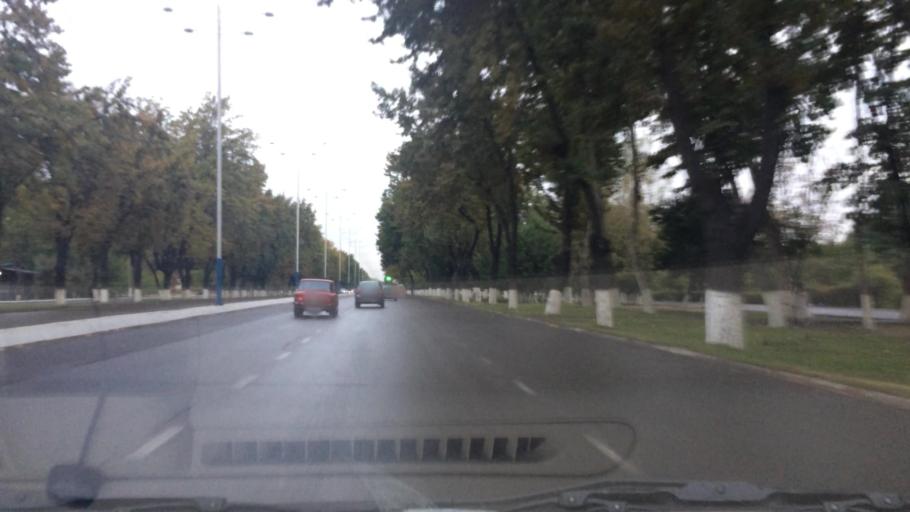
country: UZ
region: Toshkent Shahri
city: Tashkent
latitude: 41.2675
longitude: 69.2003
